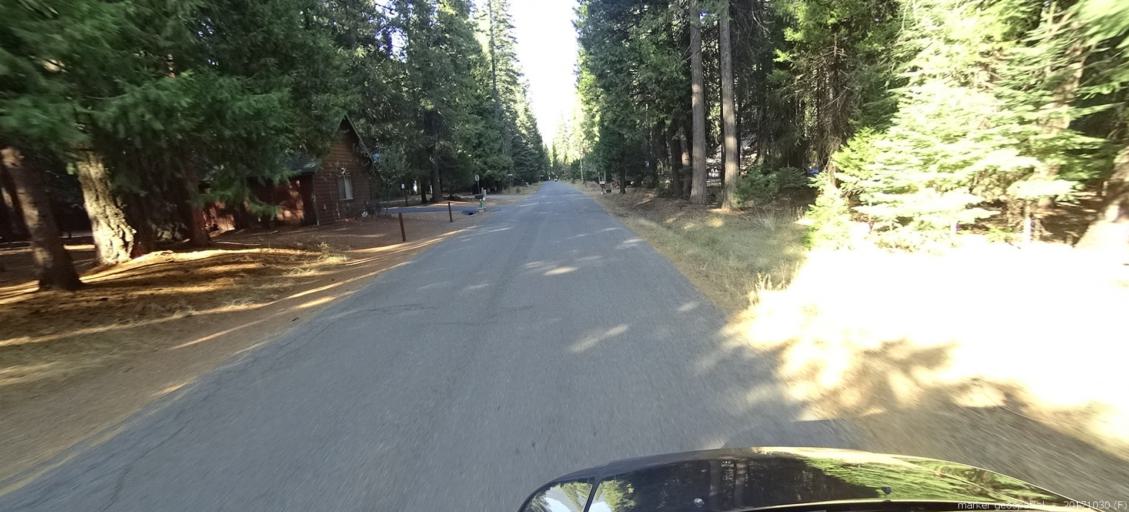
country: US
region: California
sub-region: Shasta County
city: Shingletown
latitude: 40.5557
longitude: -121.7268
